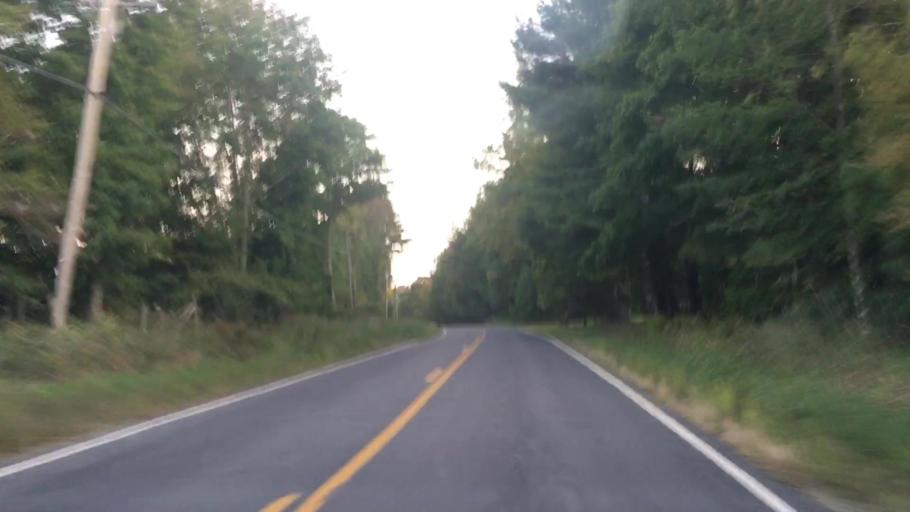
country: US
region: Maine
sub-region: Somerset County
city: Cornville
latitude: 44.8630
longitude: -69.6838
